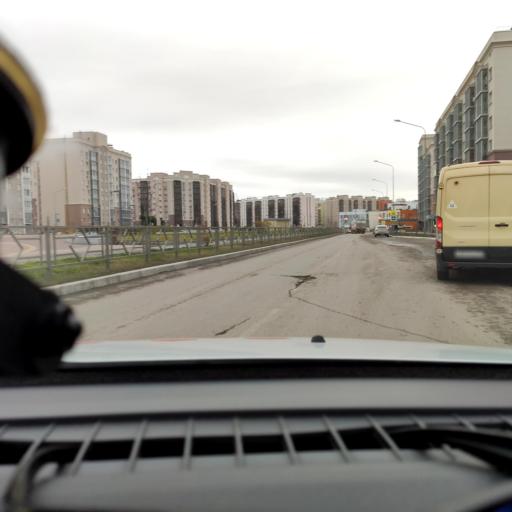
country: RU
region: Samara
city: Samara
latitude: 53.1132
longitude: 50.1458
